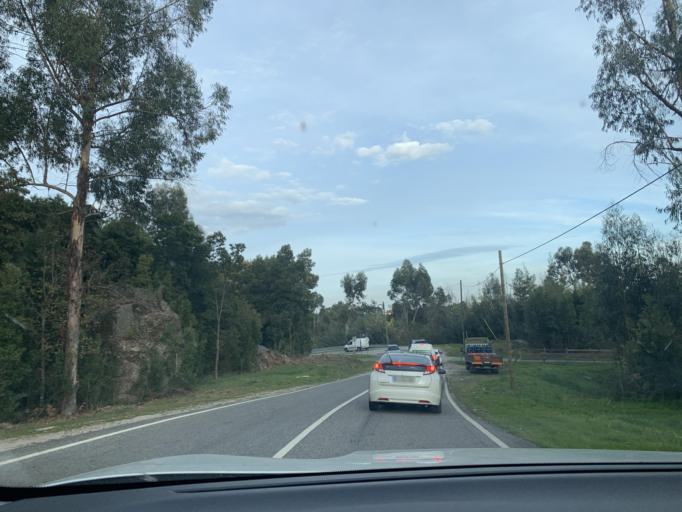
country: PT
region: Viseu
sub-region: Concelho de Tondela
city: Tondela
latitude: 40.5879
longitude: -8.0121
